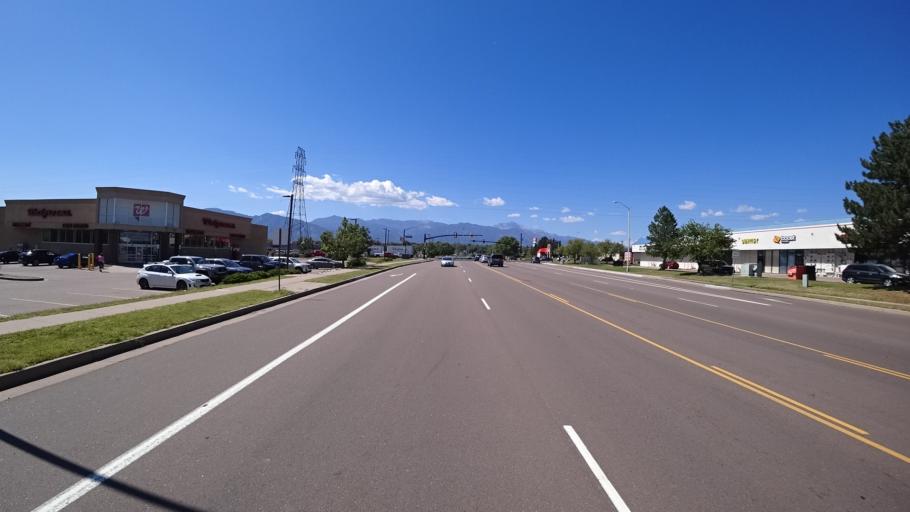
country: US
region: Colorado
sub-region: El Paso County
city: Stratmoor
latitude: 38.8048
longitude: -104.7563
